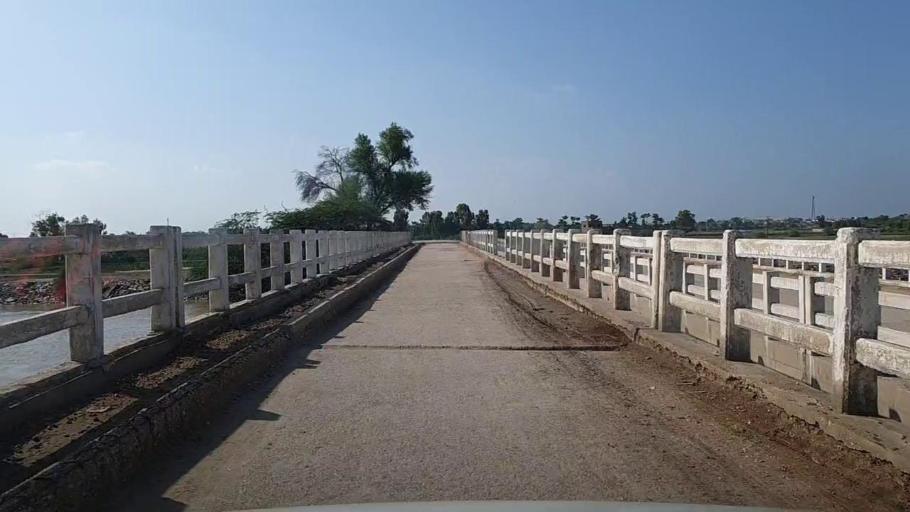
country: PK
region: Sindh
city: Kandiaro
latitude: 27.0730
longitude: 68.3132
